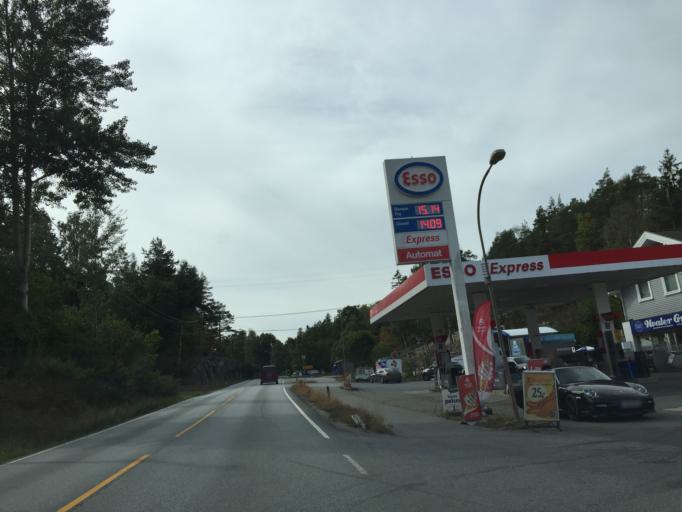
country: NO
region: Ostfold
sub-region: Fredrikstad
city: Fredrikstad
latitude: 59.1060
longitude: 10.9054
